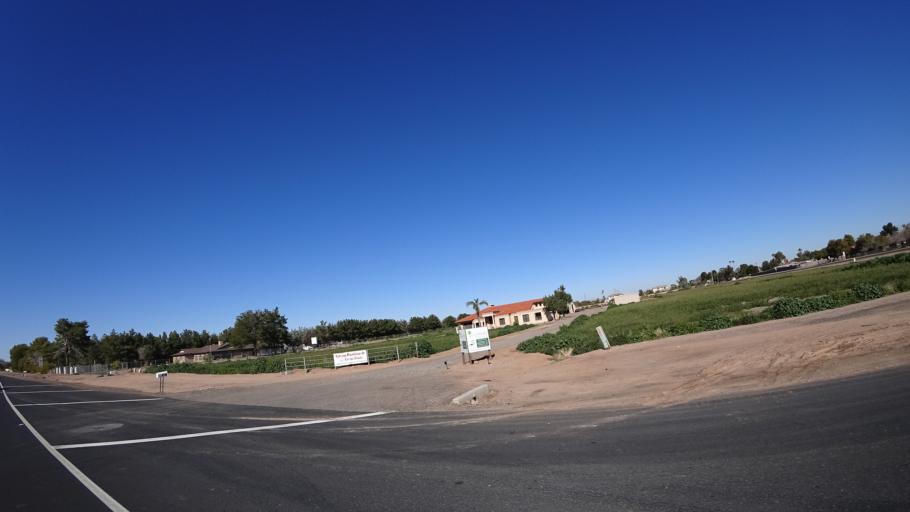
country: US
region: Arizona
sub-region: Maricopa County
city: Laveen
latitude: 33.3774
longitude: -112.2031
